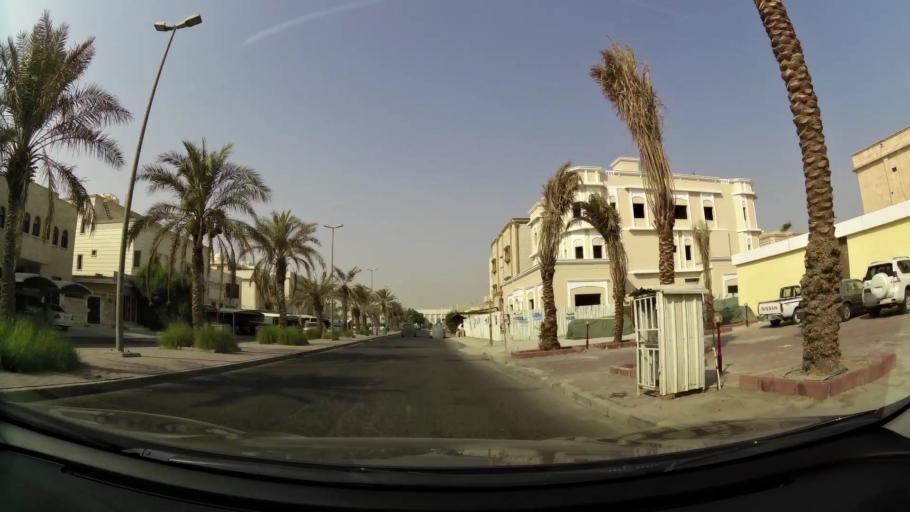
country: KW
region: Al Asimah
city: Ar Rabiyah
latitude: 29.2709
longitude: 47.8789
